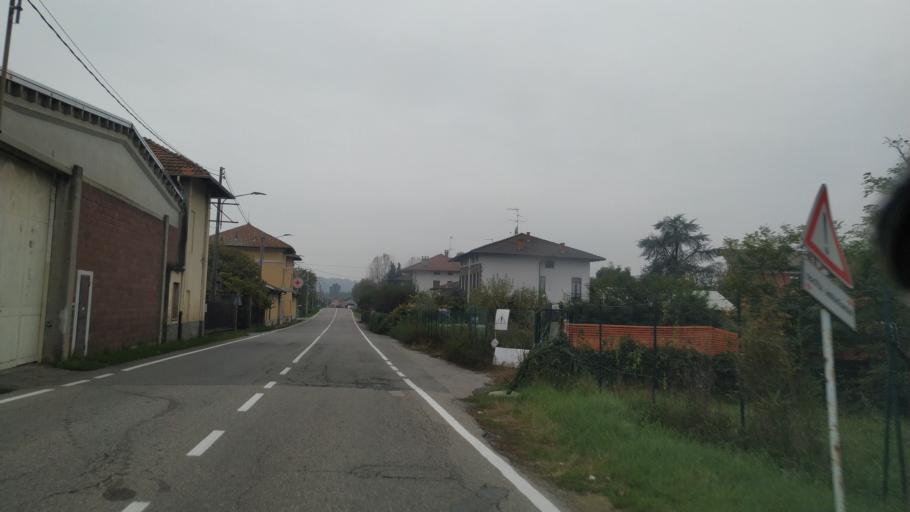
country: IT
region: Piedmont
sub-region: Provincia di Biella
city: Cossato
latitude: 45.5625
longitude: 8.1770
